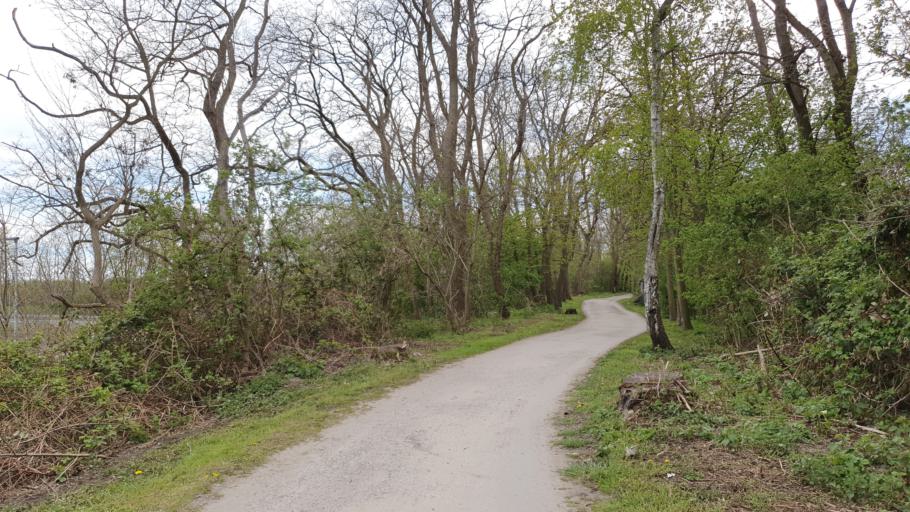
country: DE
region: North Rhine-Westphalia
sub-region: Regierungsbezirk Dusseldorf
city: Oberhausen
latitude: 51.5015
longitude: 6.8463
